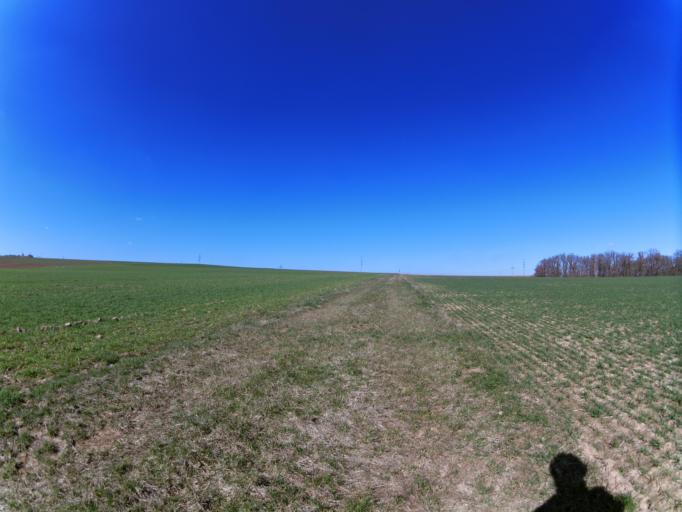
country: DE
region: Bavaria
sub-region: Regierungsbezirk Unterfranken
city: Greussenheim
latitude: 49.8032
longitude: 9.7825
